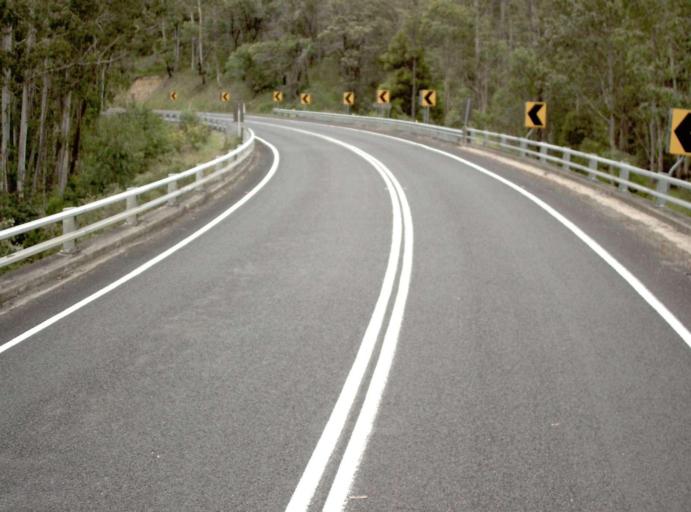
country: AU
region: New South Wales
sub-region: Bombala
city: Bombala
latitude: -37.2947
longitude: 149.2138
